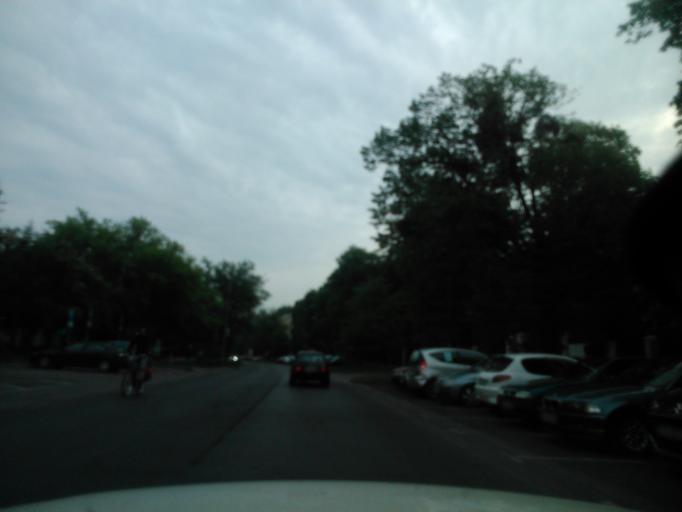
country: PL
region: Kujawsko-Pomorskie
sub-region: Torun
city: Torun
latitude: 53.0178
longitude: 18.6064
